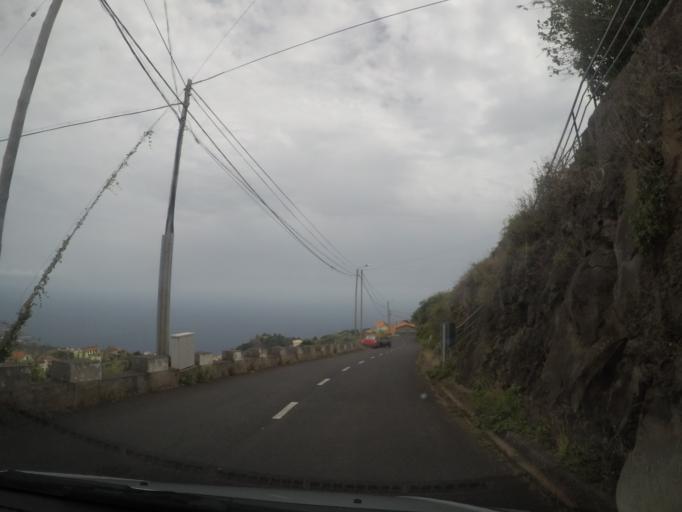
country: PT
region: Madeira
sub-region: Santa Cruz
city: Santa Cruz
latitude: 32.6864
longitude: -16.8119
